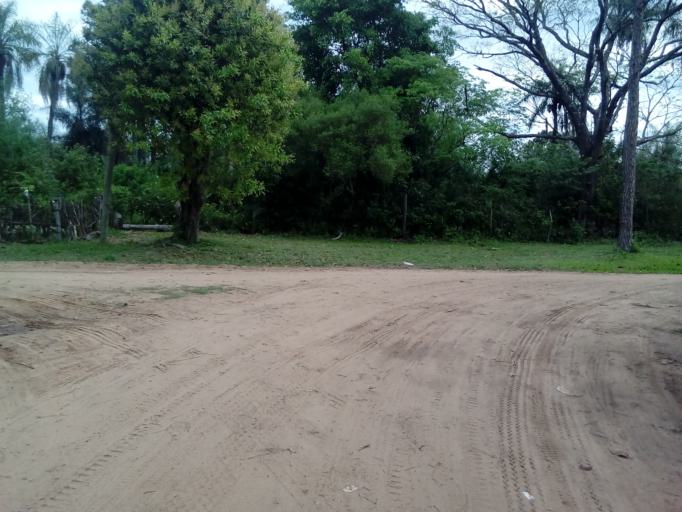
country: AR
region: Corrientes
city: San Luis del Palmar
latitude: -27.4585
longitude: -58.6586
